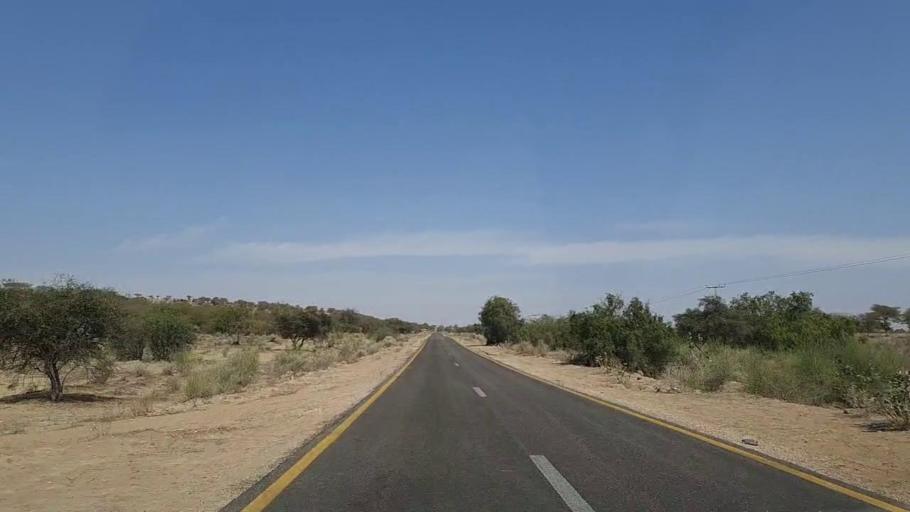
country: PK
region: Sindh
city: Mithi
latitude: 24.8926
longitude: 69.8788
